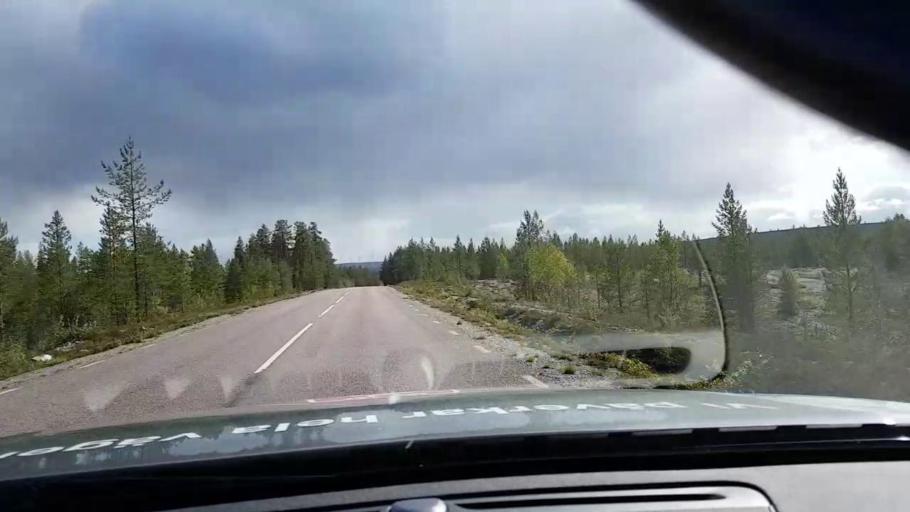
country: SE
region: Vaesterbotten
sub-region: Asele Kommun
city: Asele
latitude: 63.8857
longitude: 17.3522
